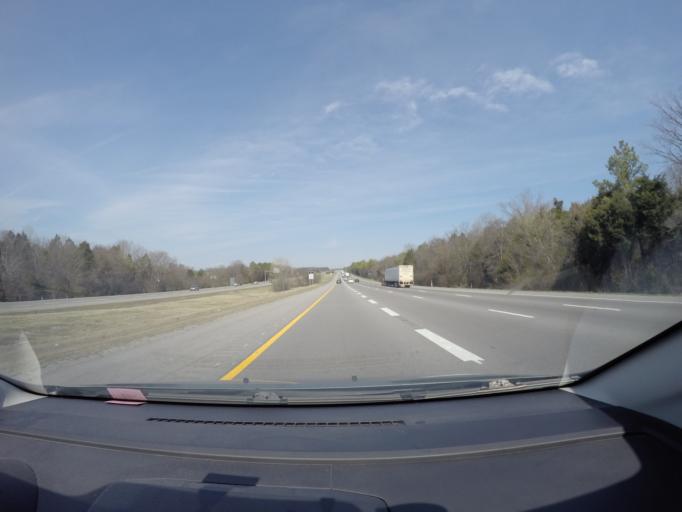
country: US
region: Tennessee
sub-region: Rutherford County
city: Smyrna
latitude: 35.9456
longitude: -86.5437
